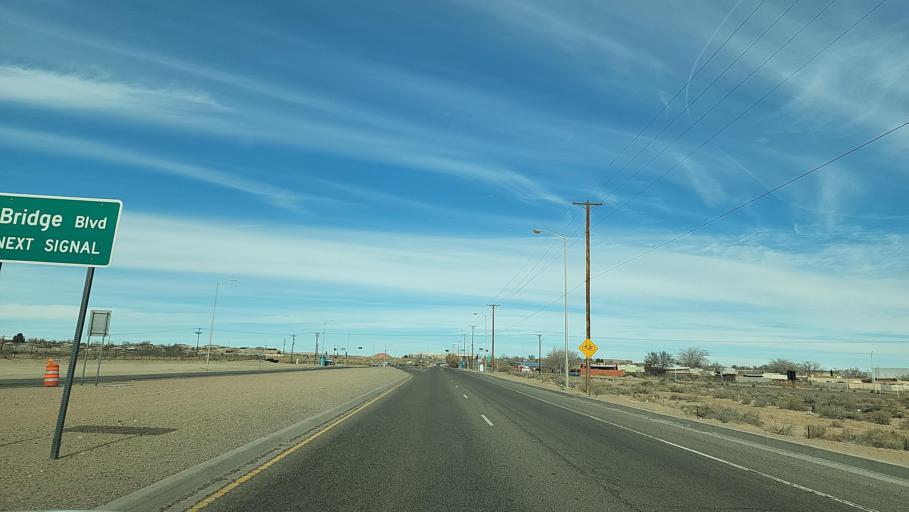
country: US
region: New Mexico
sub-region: Bernalillo County
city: Albuquerque
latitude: 35.0682
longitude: -106.7110
